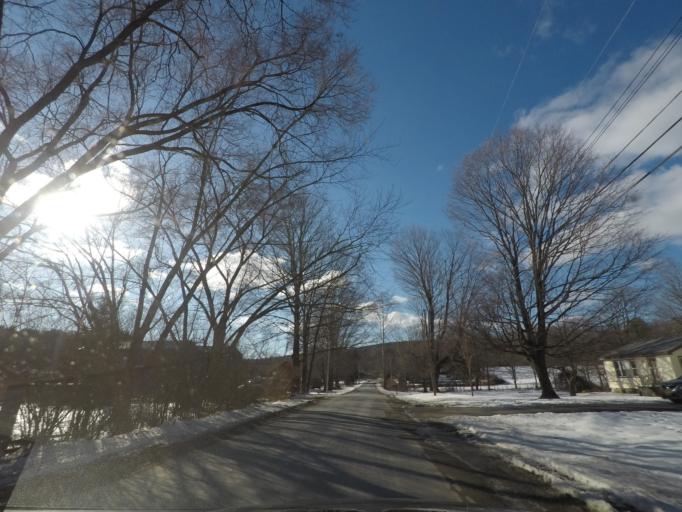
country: US
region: New York
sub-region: Rensselaer County
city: Nassau
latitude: 42.5161
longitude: -73.5158
